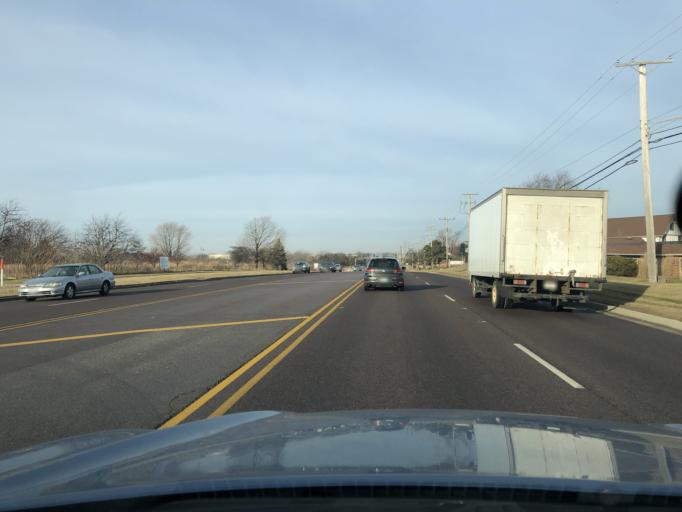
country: US
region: Illinois
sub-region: Cook County
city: Rolling Meadows
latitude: 42.0693
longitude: -88.0467
